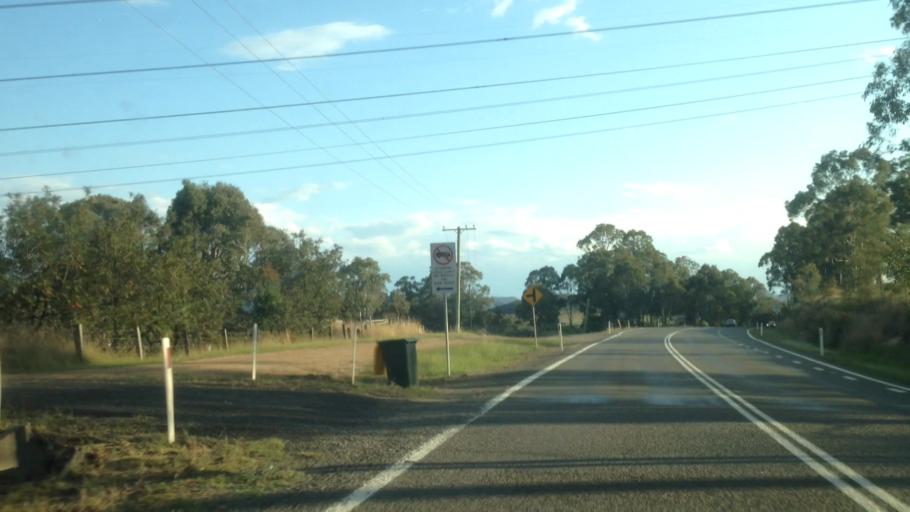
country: AU
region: New South Wales
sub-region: Cessnock
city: Kurri Kurri
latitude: -32.8707
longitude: 151.4789
